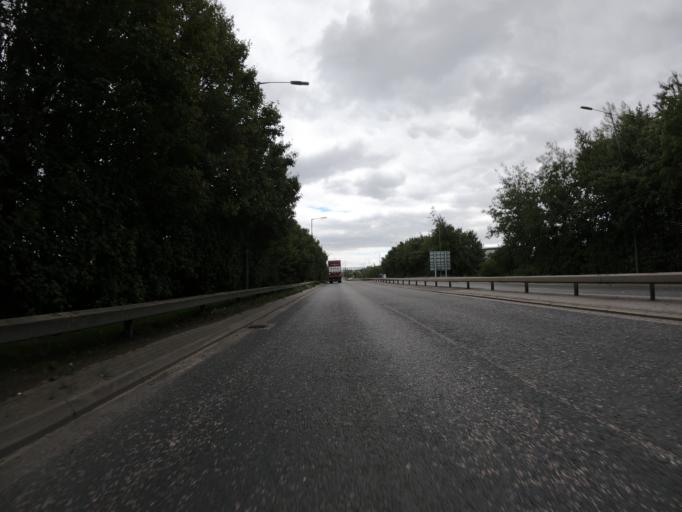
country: GB
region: England
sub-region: Greater London
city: Belvedere
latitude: 51.4963
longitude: 0.1591
